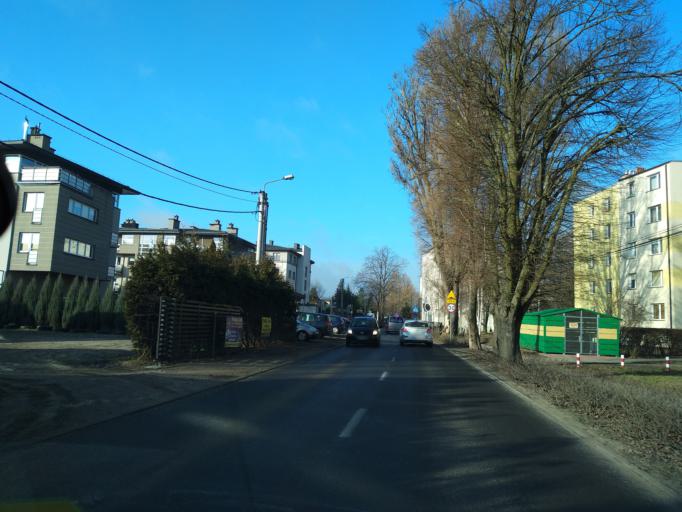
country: PL
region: Masovian Voivodeship
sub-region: Powiat piaseczynski
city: Mysiadlo
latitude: 52.0969
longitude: 21.0135
